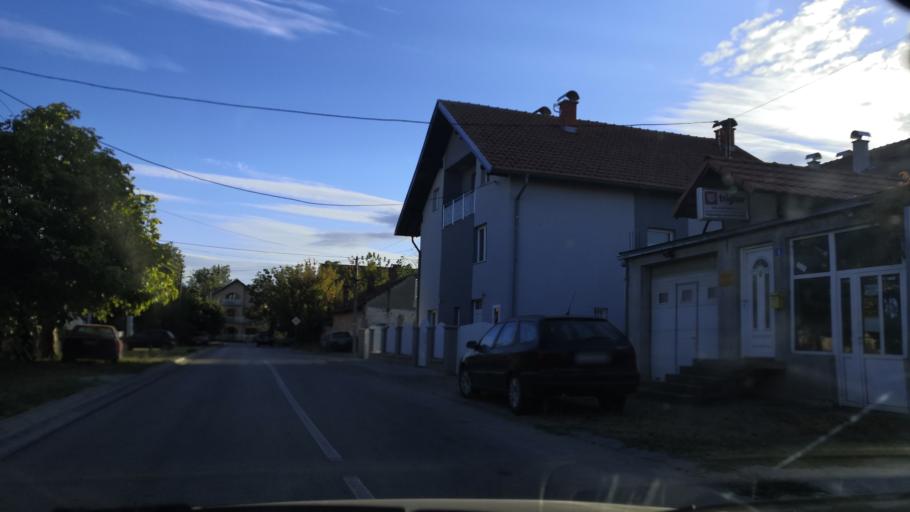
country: RS
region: Central Serbia
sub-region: Borski Okrug
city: Negotin
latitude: 44.2259
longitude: 22.5241
